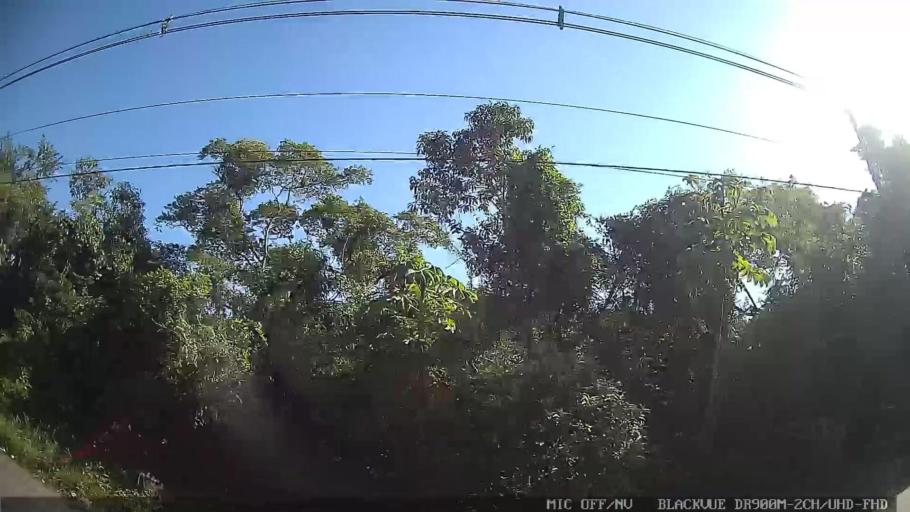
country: BR
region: Sao Paulo
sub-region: Santos
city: Santos
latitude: -23.9028
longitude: -46.3066
